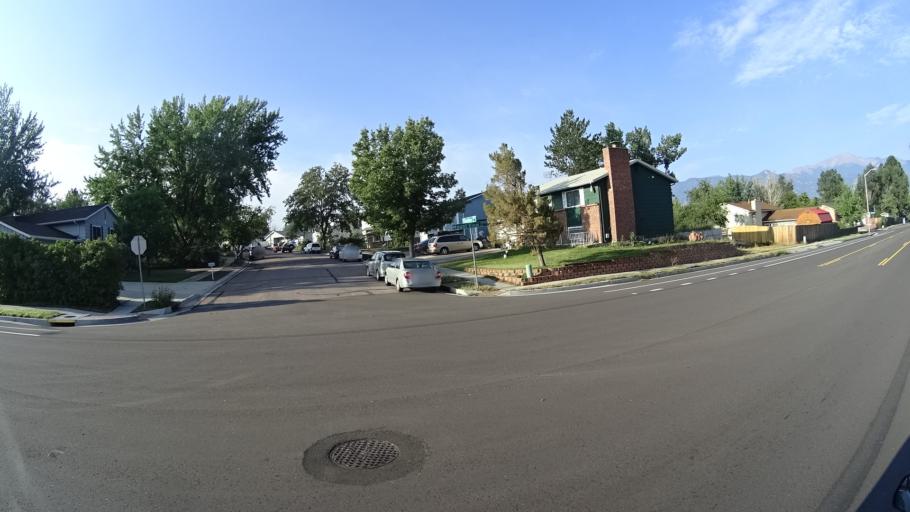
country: US
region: Colorado
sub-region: El Paso County
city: Colorado Springs
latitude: 38.8896
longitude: -104.8085
